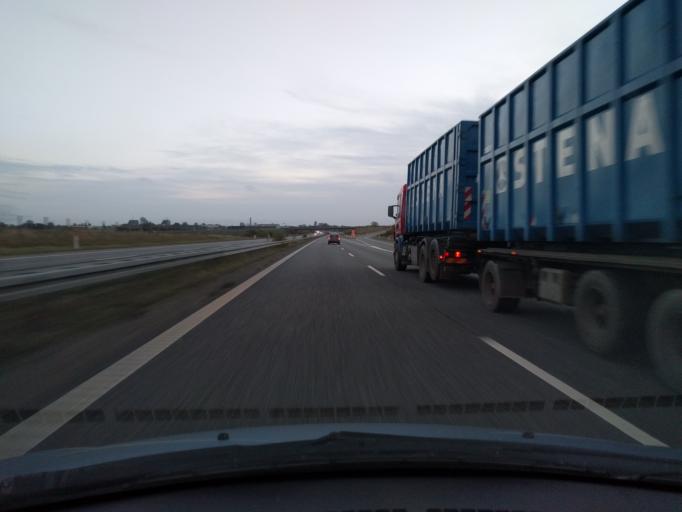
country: DK
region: South Denmark
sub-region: Faaborg-Midtfyn Kommune
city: Ringe
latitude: 55.2611
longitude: 10.4698
